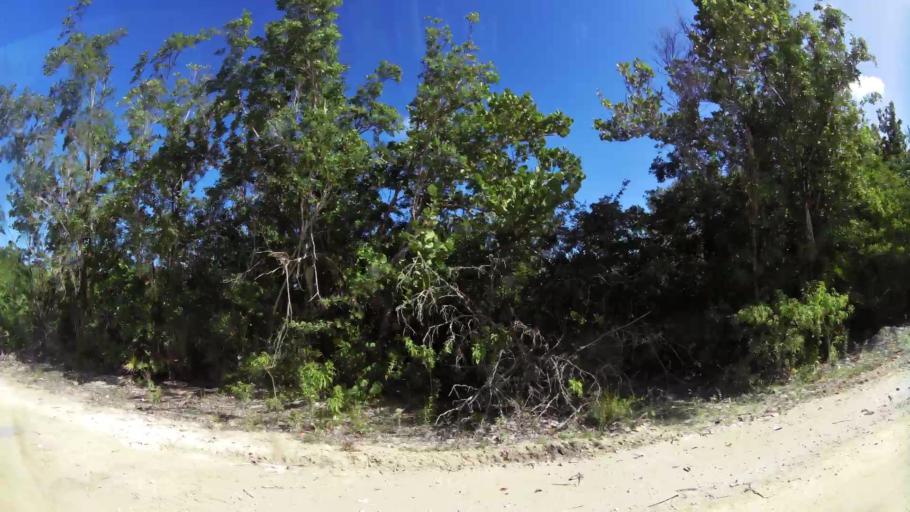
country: AG
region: Barbuda
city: Codrington
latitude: 17.5978
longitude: -61.8292
